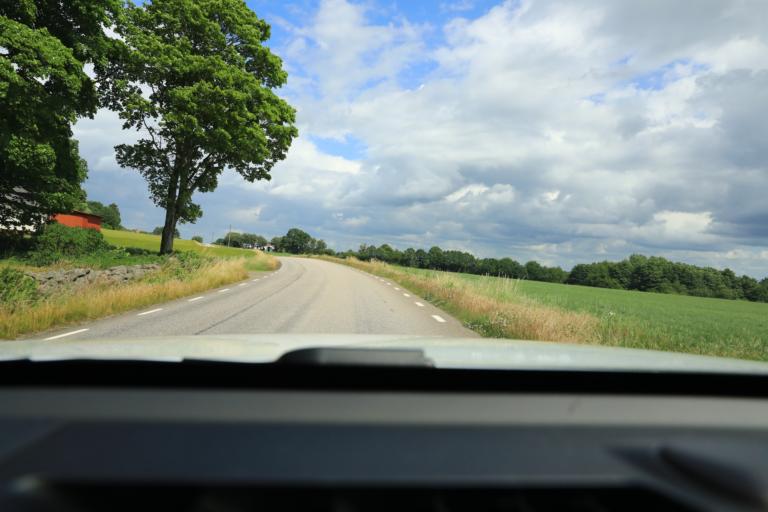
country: SE
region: Halland
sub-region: Varbergs Kommun
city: Tvaaker
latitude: 57.0881
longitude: 12.4071
